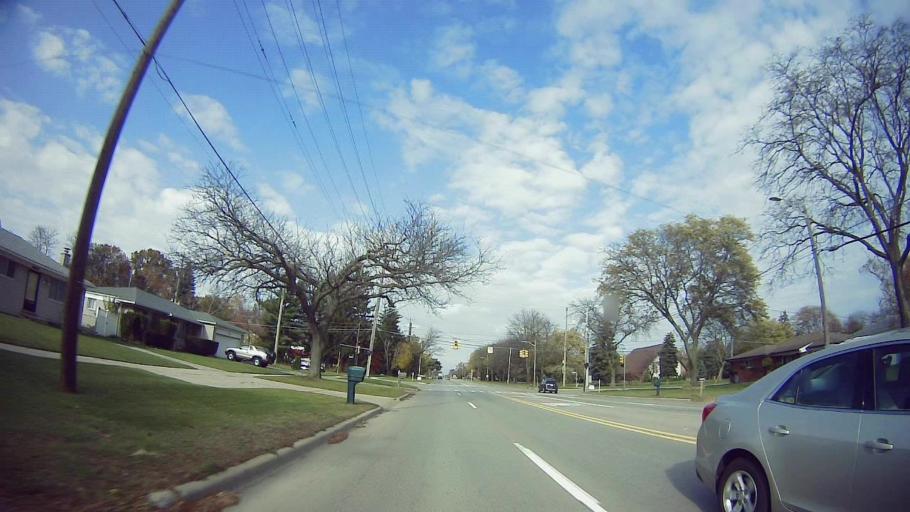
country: US
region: Michigan
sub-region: Oakland County
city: Madison Heights
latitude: 42.4984
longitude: -83.0673
